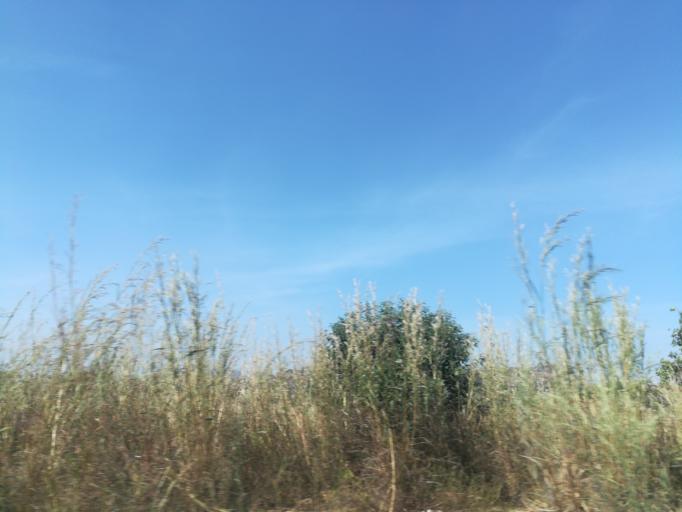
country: NG
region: Plateau
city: Bukuru
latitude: 9.7528
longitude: 8.9076
